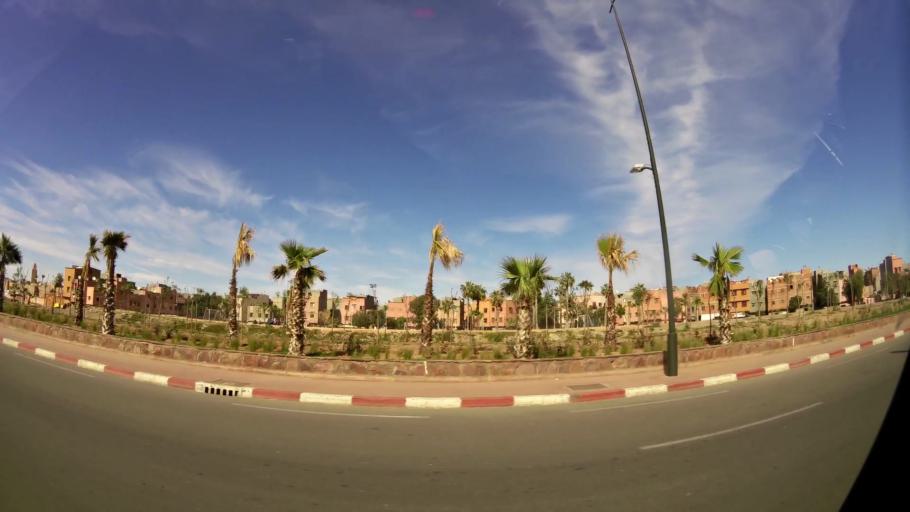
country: MA
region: Marrakech-Tensift-Al Haouz
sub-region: Marrakech
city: Marrakesh
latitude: 31.6365
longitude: -7.9794
